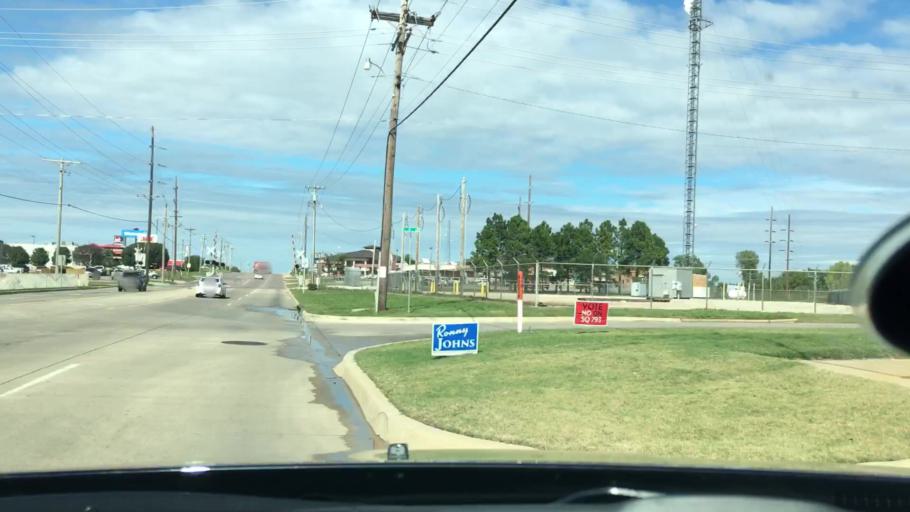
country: US
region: Oklahoma
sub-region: Pontotoc County
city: Ada
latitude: 34.7871
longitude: -96.6523
